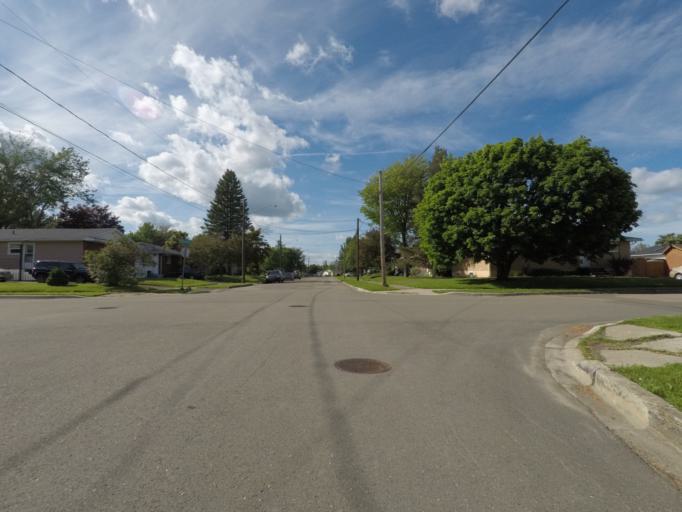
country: CA
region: New Brunswick
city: Moncton
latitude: 46.1019
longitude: -64.8260
